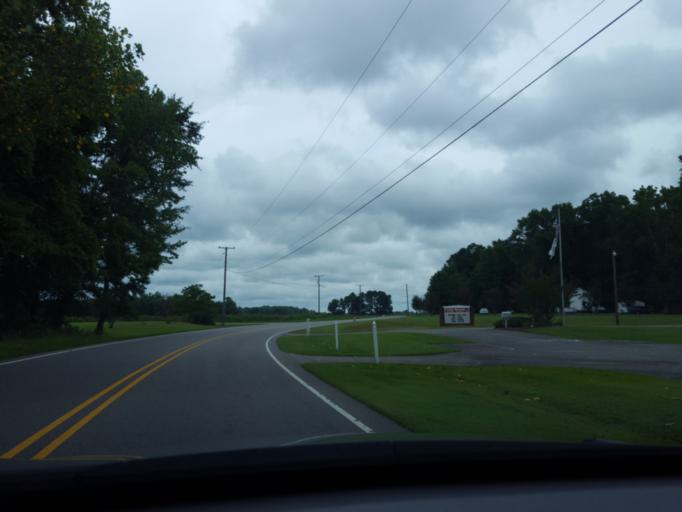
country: US
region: North Carolina
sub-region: Martin County
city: Williamston
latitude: 35.7875
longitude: -76.9069
